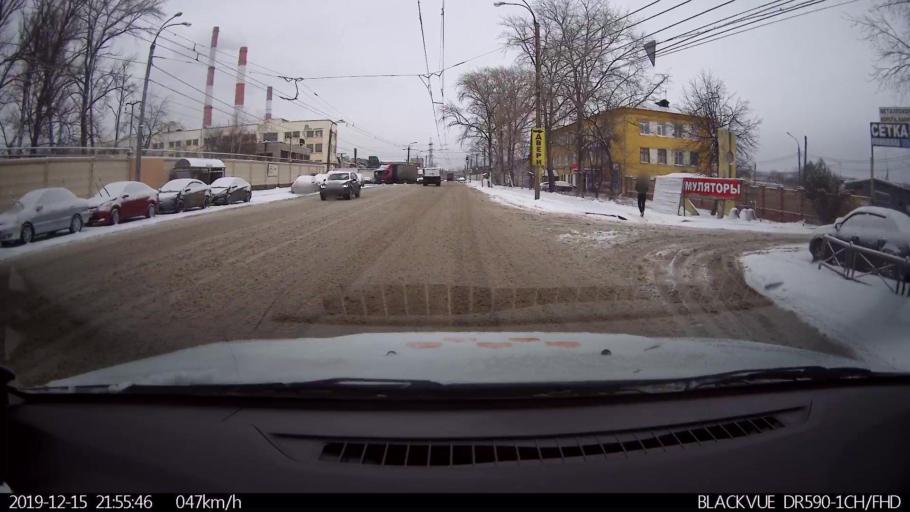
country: RU
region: Nizjnij Novgorod
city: Burevestnik
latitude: 56.2372
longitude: 43.8859
